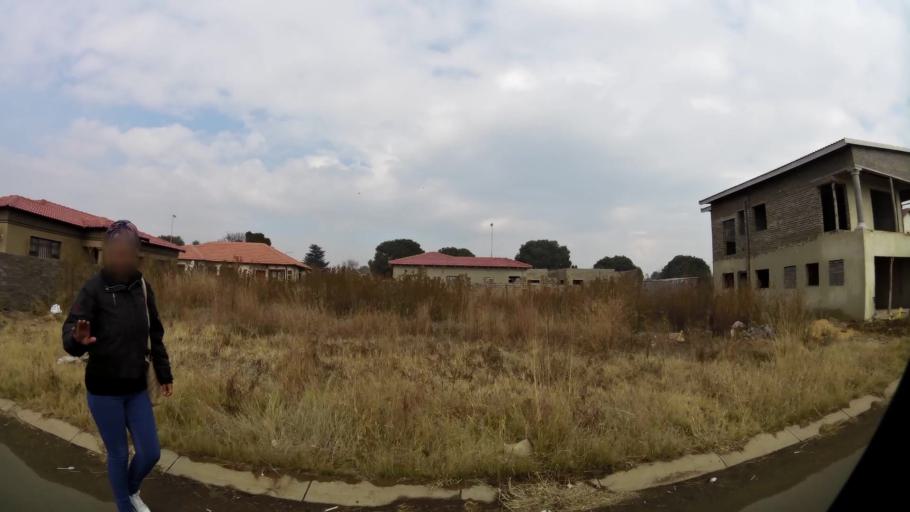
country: ZA
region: Gauteng
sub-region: Sedibeng District Municipality
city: Vanderbijlpark
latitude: -26.6850
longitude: 27.8496
